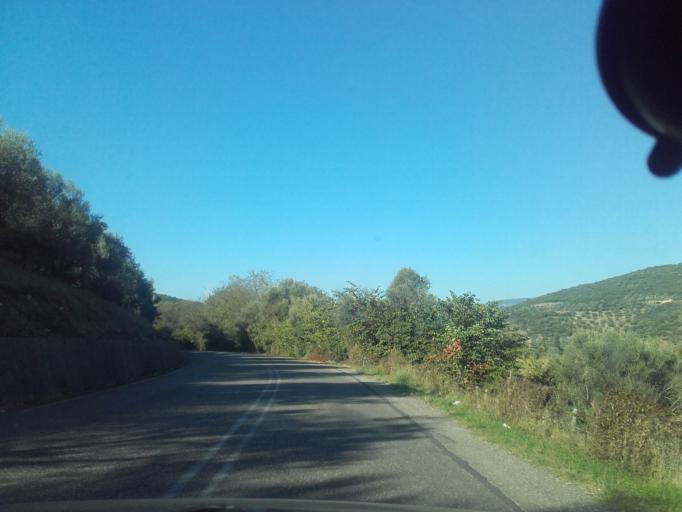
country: GR
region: West Greece
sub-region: Nomos Aitolias kai Akarnanias
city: Nafpaktos
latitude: 38.4184
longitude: 21.9172
